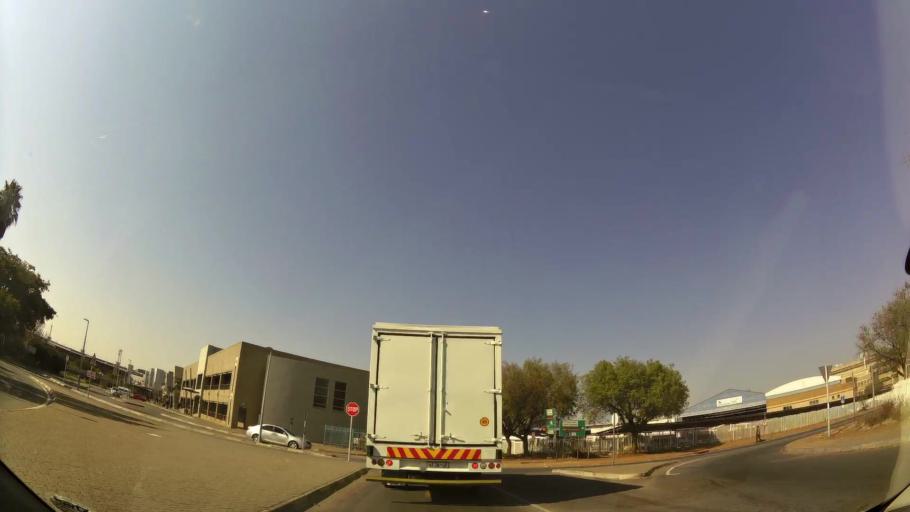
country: ZA
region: Gauteng
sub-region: City of Johannesburg Metropolitan Municipality
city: Modderfontein
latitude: -26.1354
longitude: 28.2265
